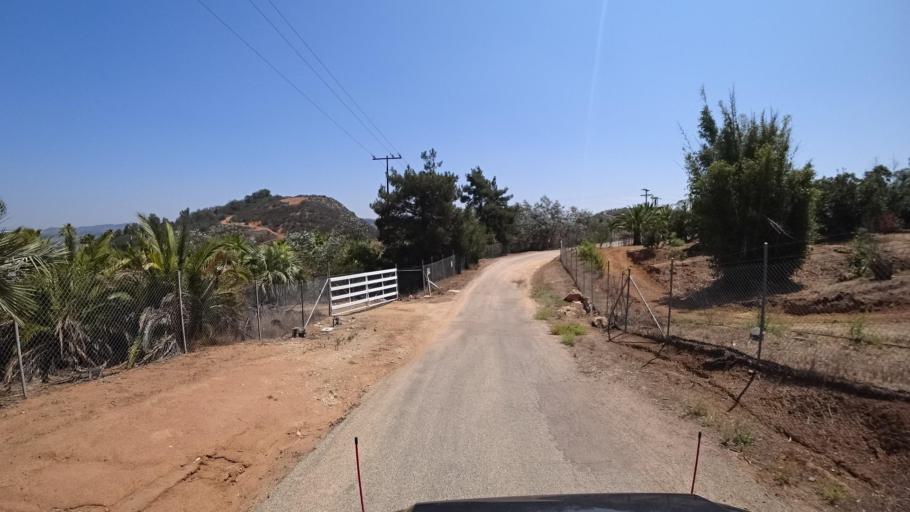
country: US
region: California
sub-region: San Diego County
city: Fallbrook
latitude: 33.4540
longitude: -117.2658
